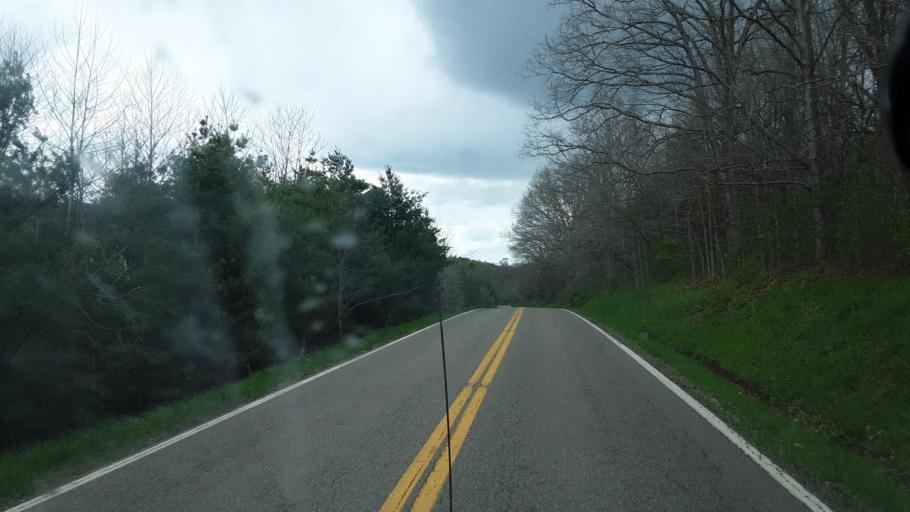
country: US
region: Ohio
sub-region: Noble County
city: Caldwell
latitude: 39.7457
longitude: -81.6189
